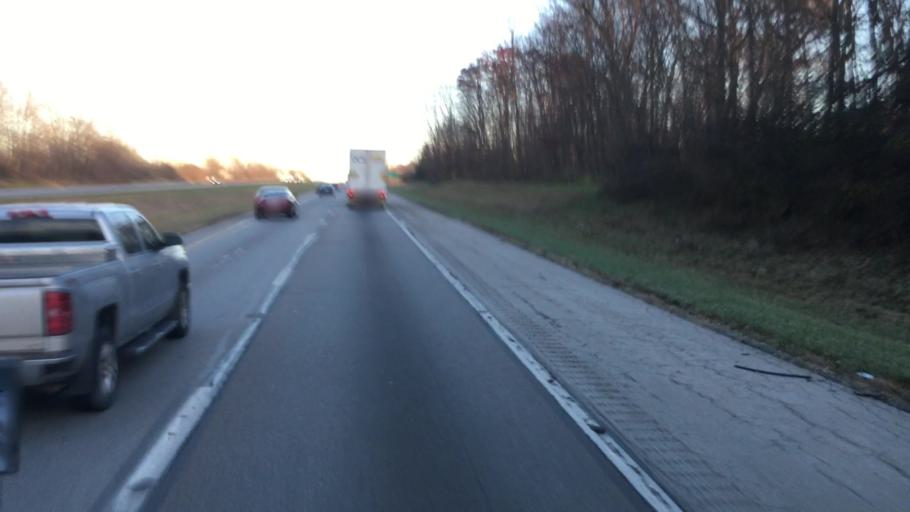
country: US
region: Ohio
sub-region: Preble County
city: Lewisburg
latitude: 39.8373
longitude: -84.5258
